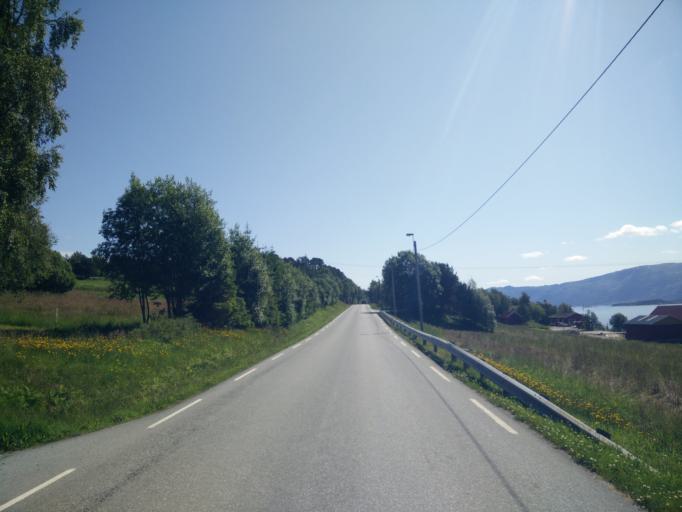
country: NO
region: More og Romsdal
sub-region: Kristiansund
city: Rensvik
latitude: 63.0285
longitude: 7.7850
